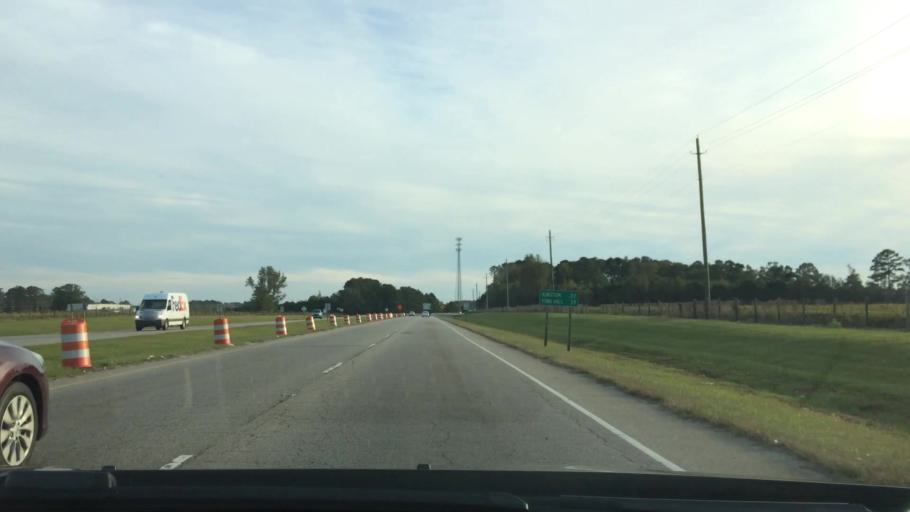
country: US
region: North Carolina
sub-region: Pitt County
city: Winterville
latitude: 35.5275
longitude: -77.4082
